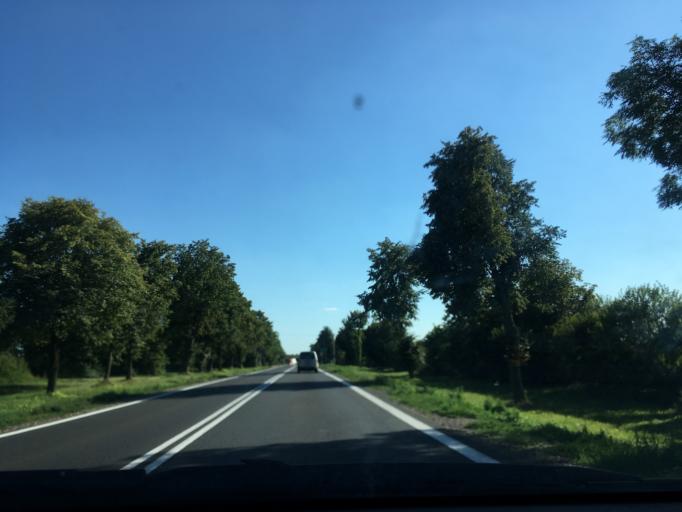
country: PL
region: Podlasie
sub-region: Powiat sokolski
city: Suchowola
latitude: 53.4743
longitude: 23.0911
